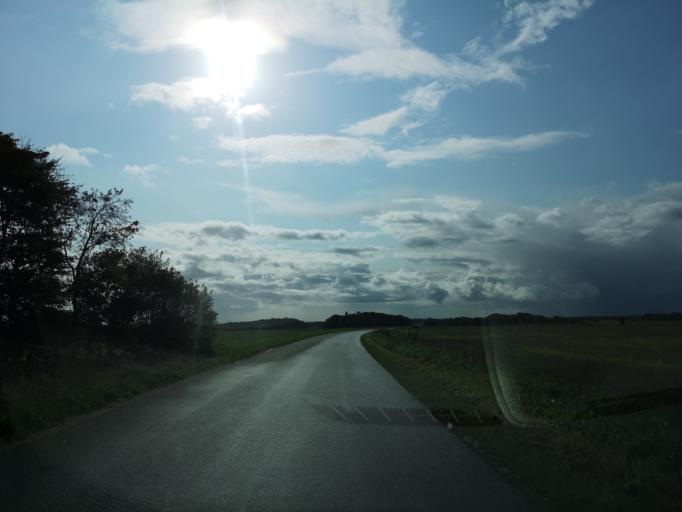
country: DK
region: Central Jutland
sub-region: Ringkobing-Skjern Kommune
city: Skjern
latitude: 55.9825
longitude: 8.5608
